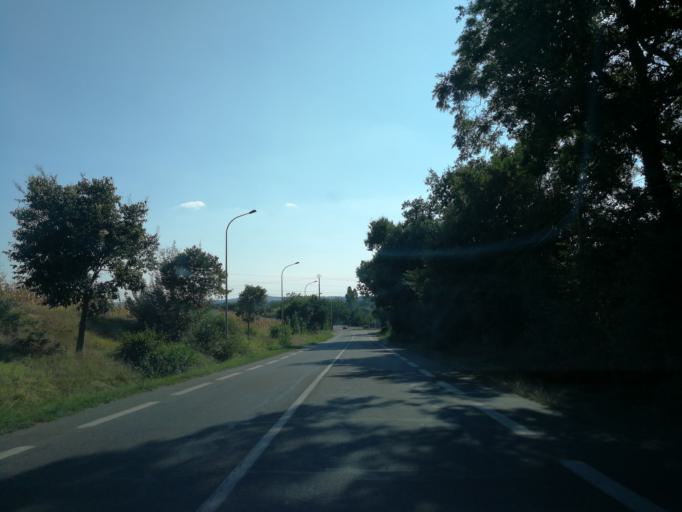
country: FR
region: Midi-Pyrenees
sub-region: Departement de la Haute-Garonne
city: Balma
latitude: 43.6097
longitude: 1.5179
